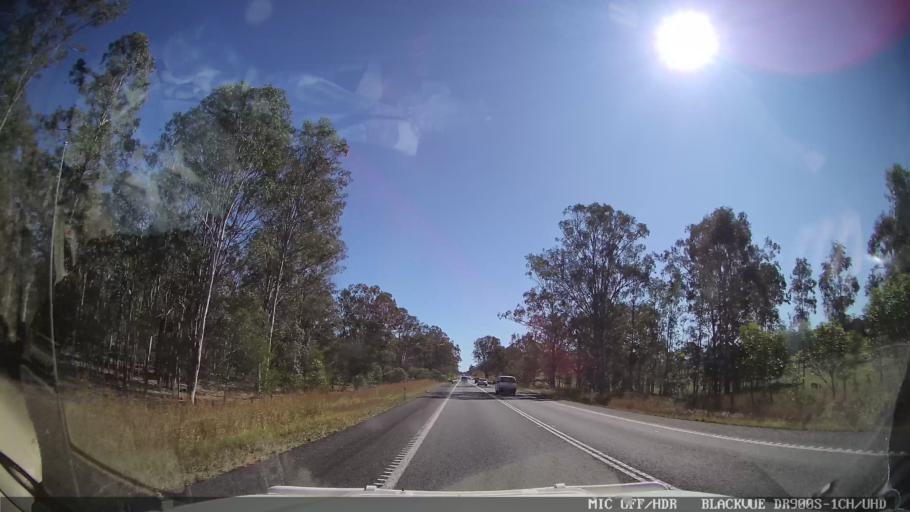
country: AU
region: Queensland
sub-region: Gympie Regional Council
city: Gympie
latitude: -26.0408
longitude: 152.5708
